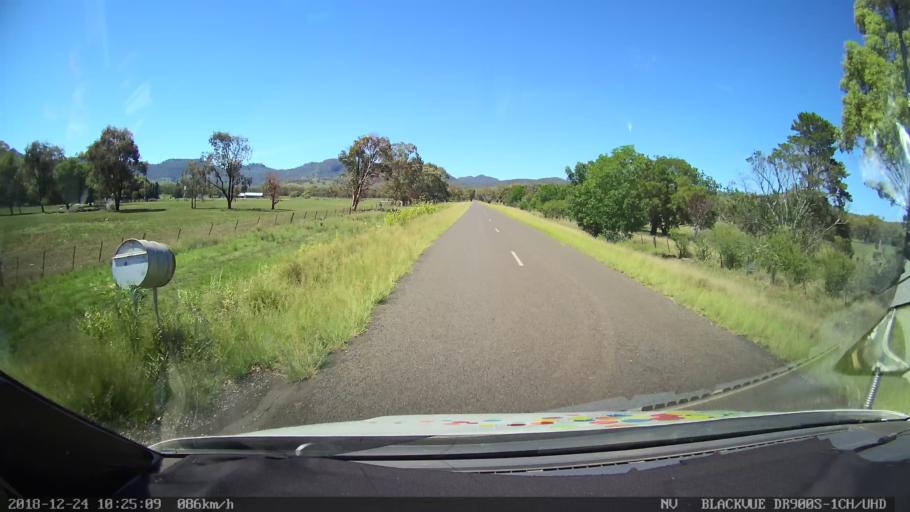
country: AU
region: New South Wales
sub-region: Liverpool Plains
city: Quirindi
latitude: -31.7955
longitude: 150.5297
